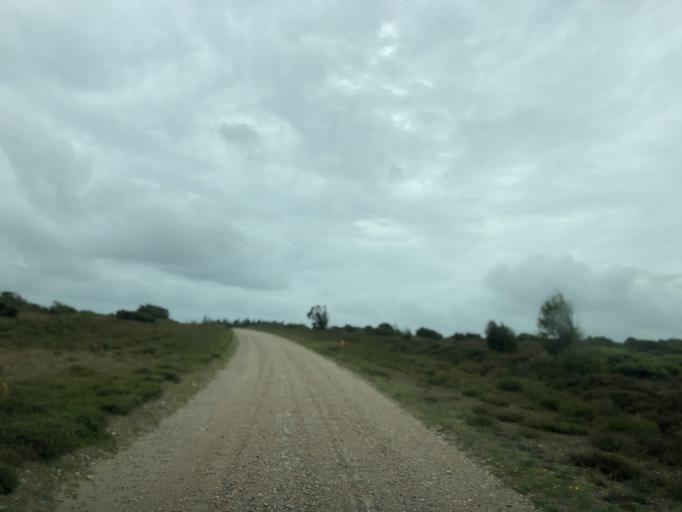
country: DK
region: Central Jutland
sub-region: Holstebro Kommune
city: Holstebro
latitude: 56.2425
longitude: 8.4955
